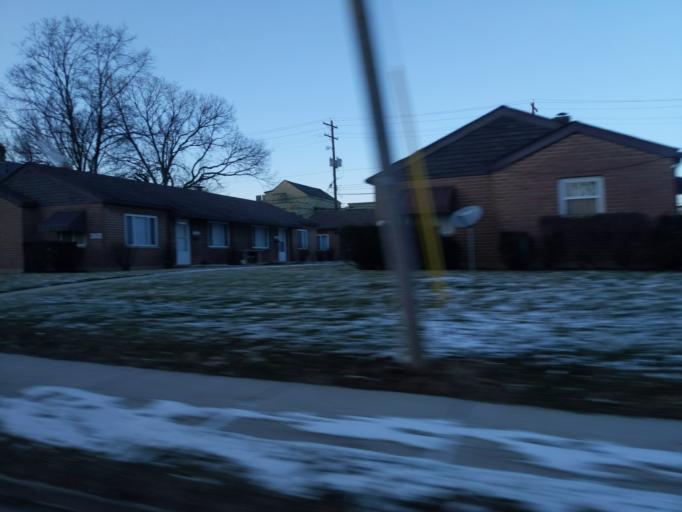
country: US
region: Ohio
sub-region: Franklin County
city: Grandview Heights
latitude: 39.9915
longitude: -83.0369
